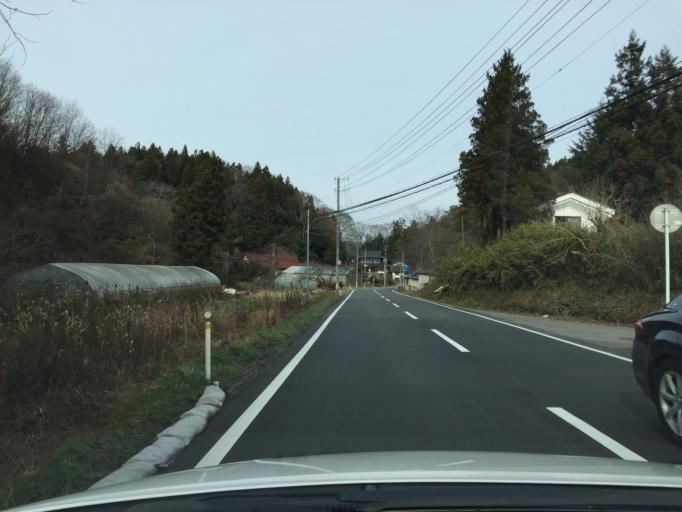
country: JP
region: Fukushima
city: Ishikawa
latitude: 37.2362
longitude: 140.6283
